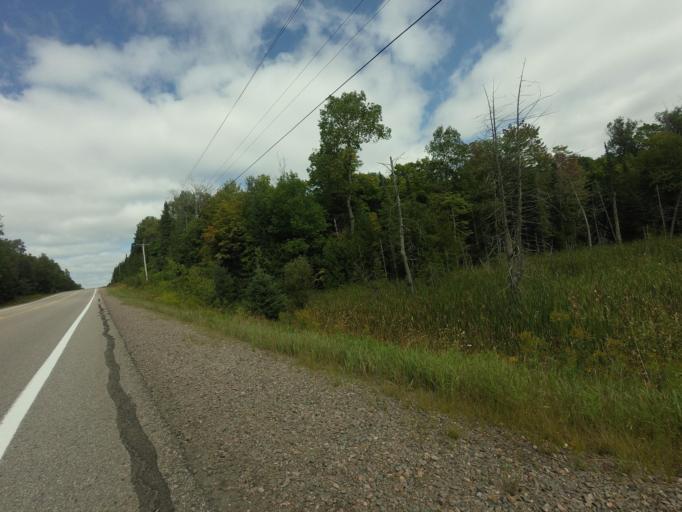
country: CA
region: Ontario
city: Bancroft
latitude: 44.9486
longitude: -78.2940
